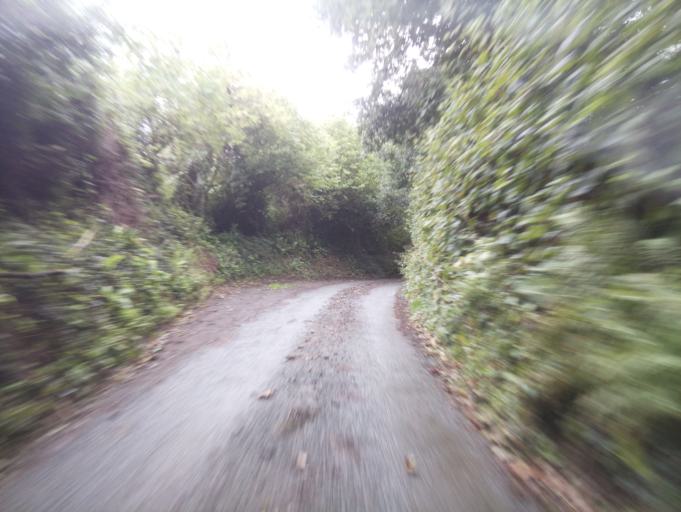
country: GB
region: England
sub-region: Devon
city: Dartmouth
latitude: 50.3456
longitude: -3.6206
